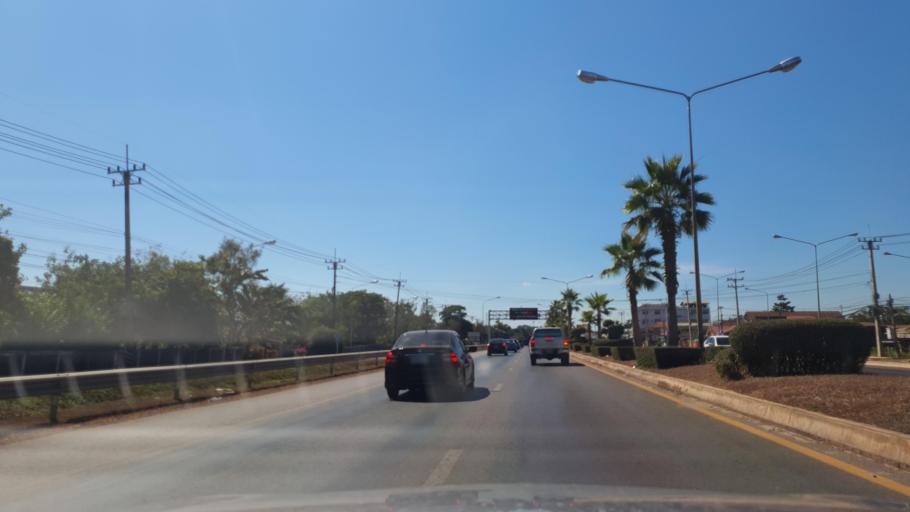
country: TH
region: Sakon Nakhon
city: Sakon Nakhon
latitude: 17.2016
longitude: 104.0995
